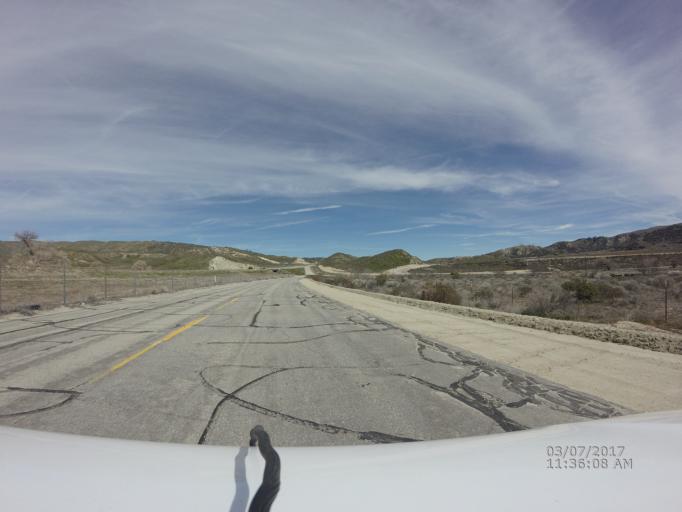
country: US
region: California
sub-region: Kern County
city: Lebec
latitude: 34.7595
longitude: -118.7941
